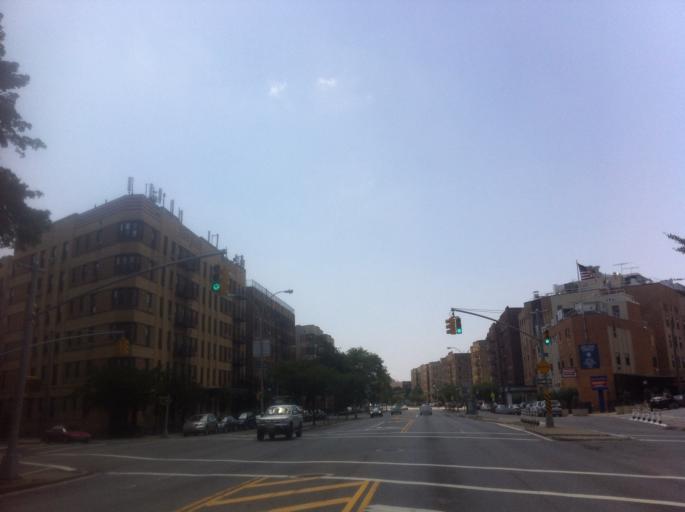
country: US
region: New York
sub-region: Kings County
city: Brooklyn
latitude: 40.6147
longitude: -73.9466
